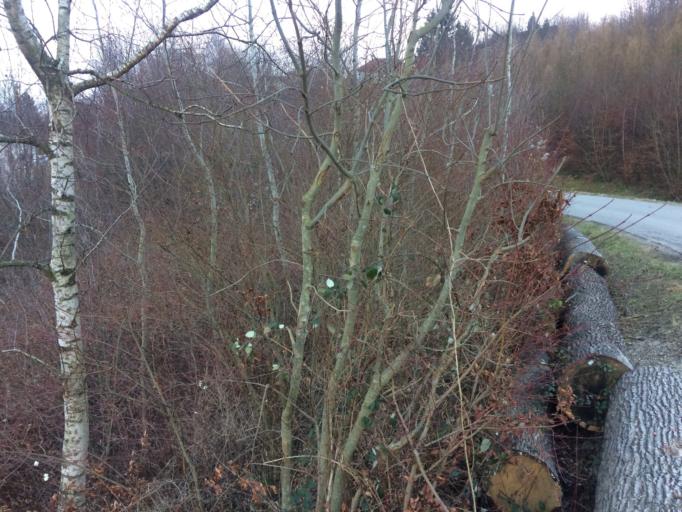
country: AT
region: Lower Austria
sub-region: Politischer Bezirk Wien-Umgebung
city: Gablitz
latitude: 48.2195
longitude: 16.1384
